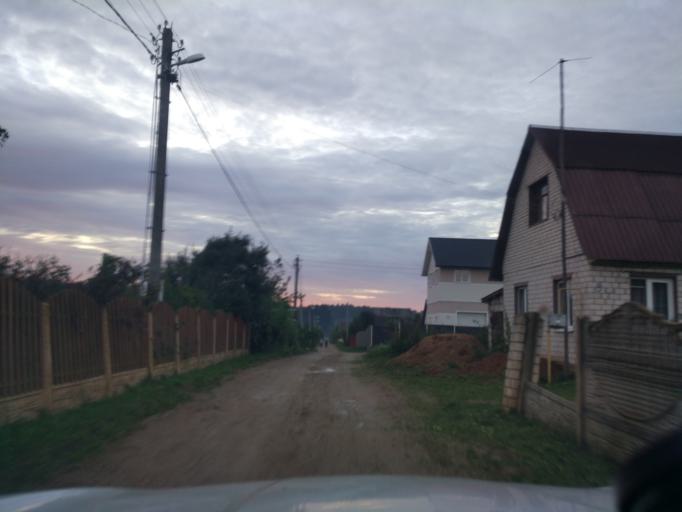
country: BY
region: Minsk
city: Astrashytski Haradok
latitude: 54.0890
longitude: 27.6979
